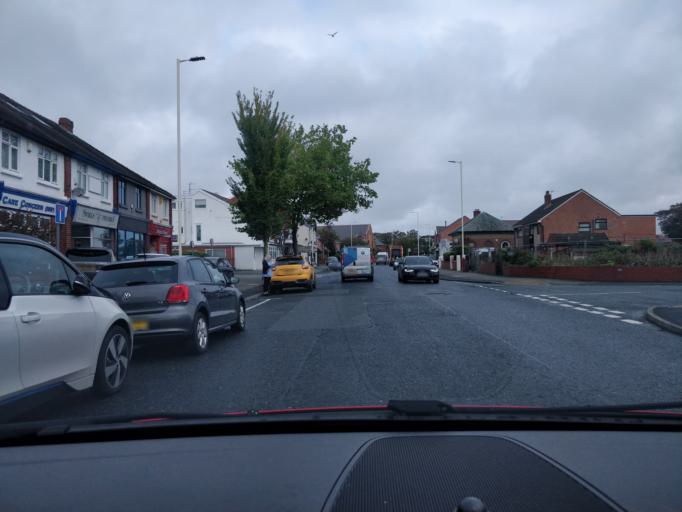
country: GB
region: England
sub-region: Sefton
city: Southport
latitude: 53.6189
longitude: -3.0157
